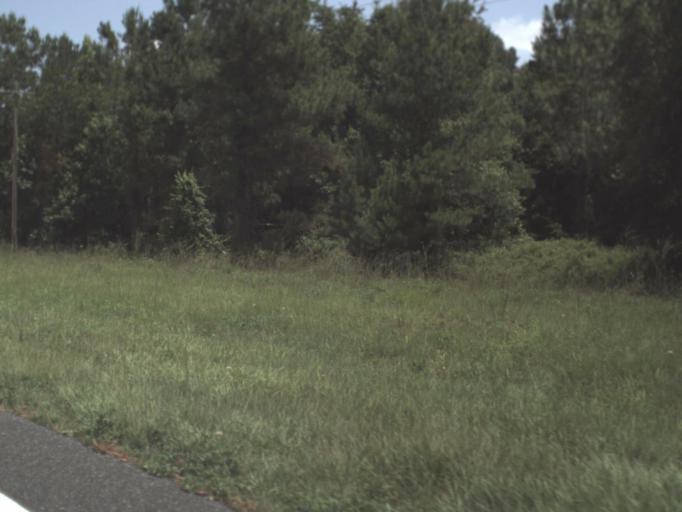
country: US
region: Florida
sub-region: Taylor County
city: Perry
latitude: 30.0091
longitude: -83.5167
